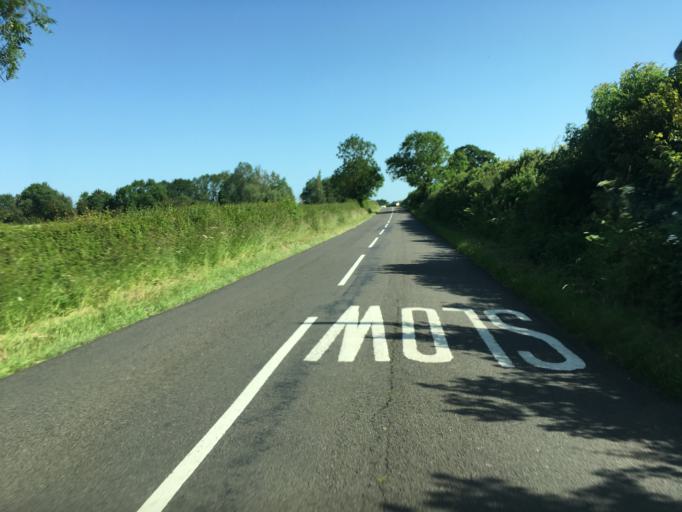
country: GB
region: England
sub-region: Buckinghamshire
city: Steeple Claydon
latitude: 51.9430
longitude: -0.9460
